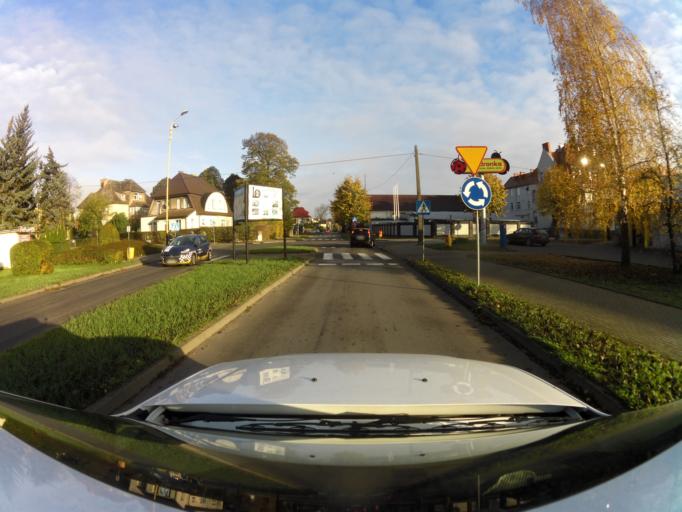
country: PL
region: West Pomeranian Voivodeship
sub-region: Powiat gryficki
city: Gryfice
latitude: 53.9134
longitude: 15.1955
